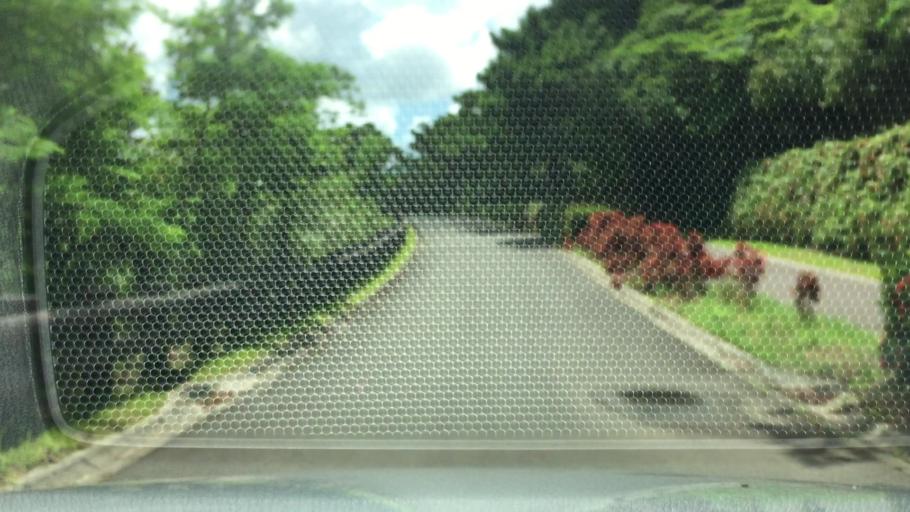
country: JP
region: Okinawa
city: Ishigaki
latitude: 24.3859
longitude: 124.1716
